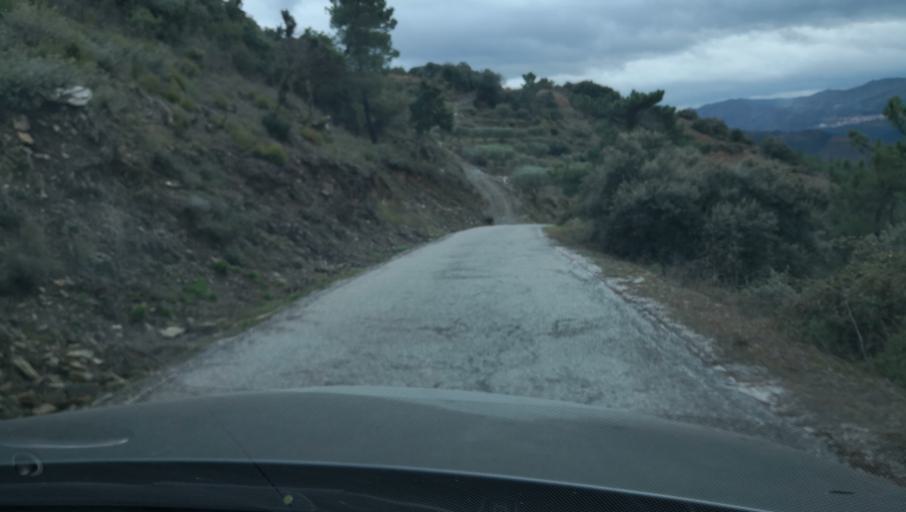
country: PT
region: Vila Real
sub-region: Sabrosa
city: Vilela
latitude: 41.1838
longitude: -7.5724
